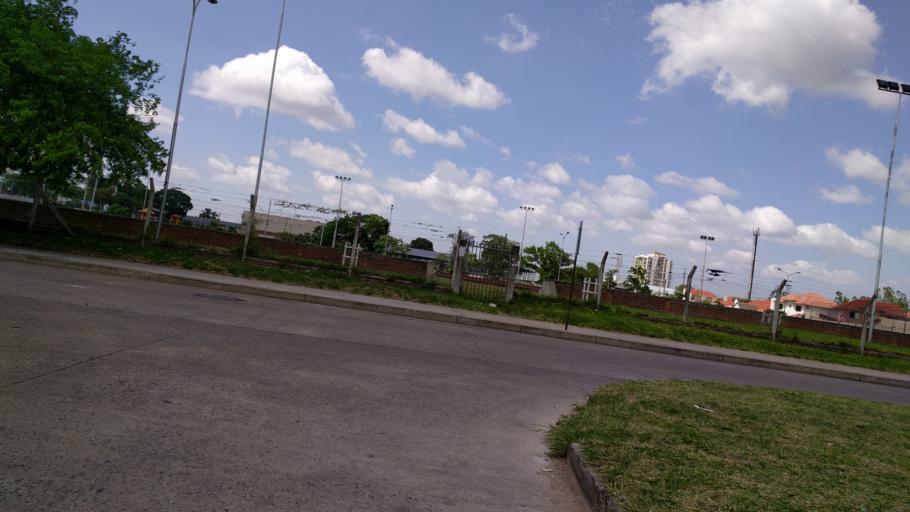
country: BO
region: Santa Cruz
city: Santa Cruz de la Sierra
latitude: -17.7810
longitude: -63.2105
